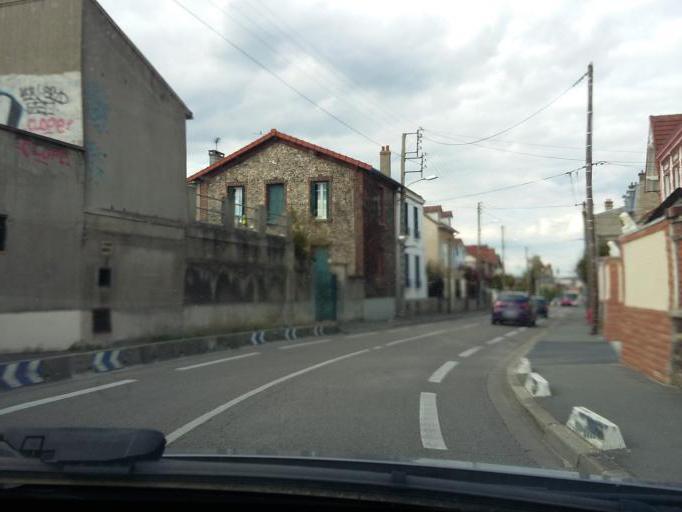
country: FR
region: Ile-de-France
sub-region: Departement du Val-d'Oise
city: Sannois
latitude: 48.9717
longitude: 2.2640
